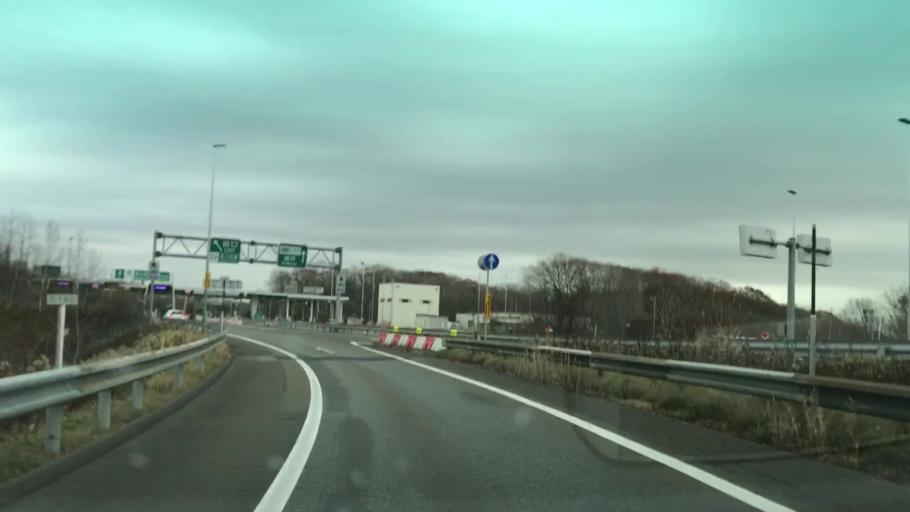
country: JP
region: Hokkaido
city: Tomakomai
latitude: 42.7099
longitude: 141.6535
